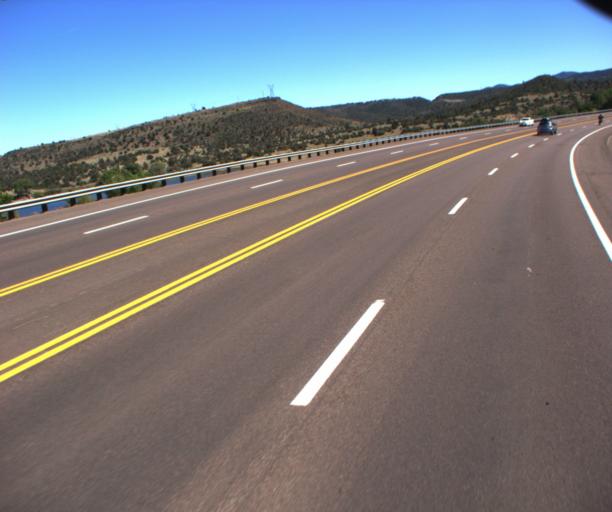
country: US
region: Arizona
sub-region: Yavapai County
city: Prescott
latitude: 34.5875
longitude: -112.4243
